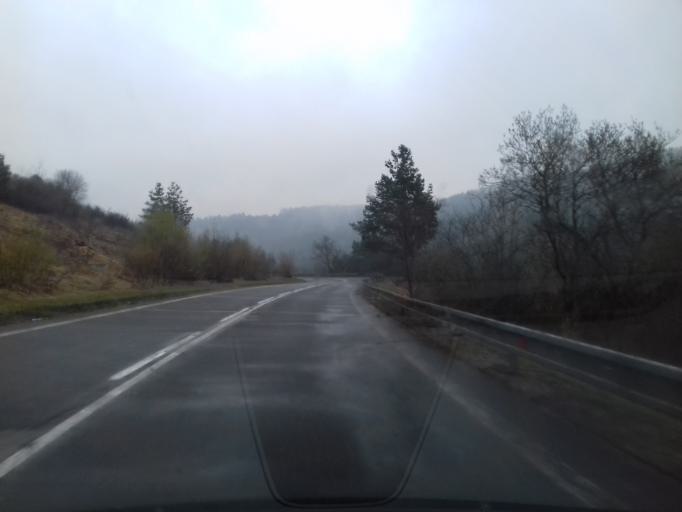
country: SK
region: Presovsky
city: Stara L'ubovna
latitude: 49.3593
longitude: 20.6981
